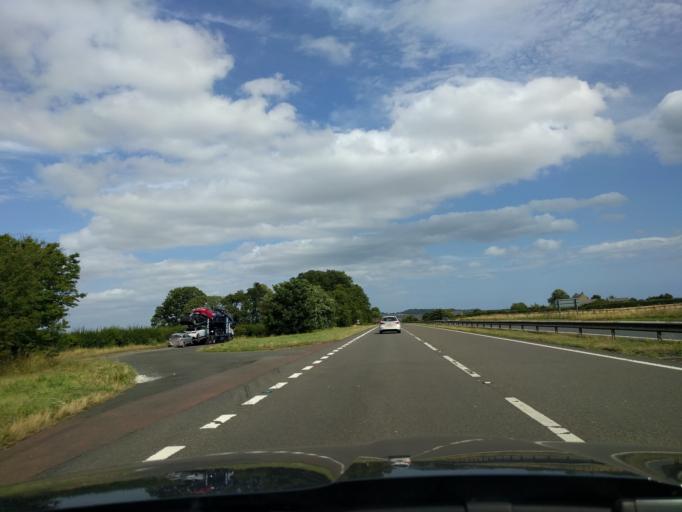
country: GB
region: England
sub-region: Northumberland
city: Alnwick
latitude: 55.3930
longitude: -1.7036
